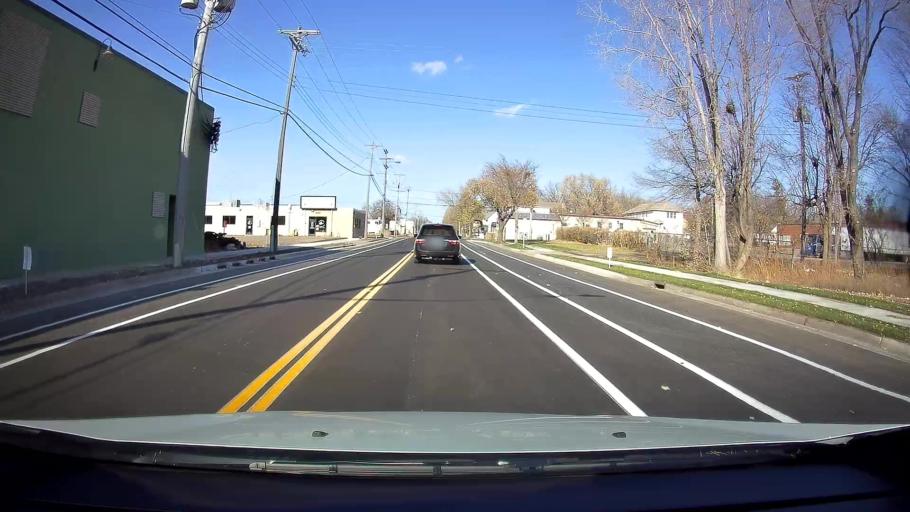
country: US
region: Minnesota
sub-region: Ramsey County
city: Falcon Heights
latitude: 44.9584
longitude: -93.1773
